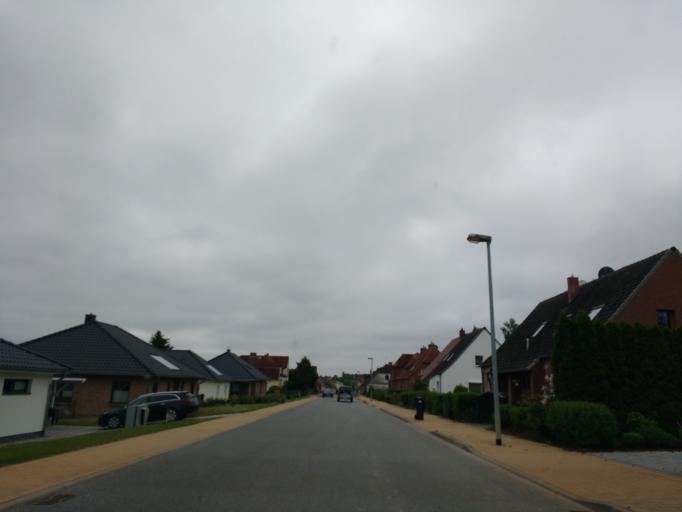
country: DE
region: Mecklenburg-Vorpommern
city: Neukloster
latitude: 53.8698
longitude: 11.6766
